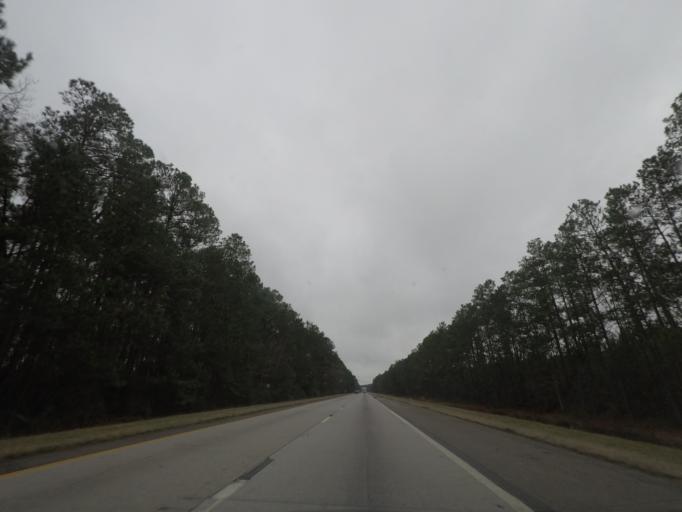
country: US
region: South Carolina
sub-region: Colleton County
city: Walterboro
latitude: 33.0595
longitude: -80.6645
